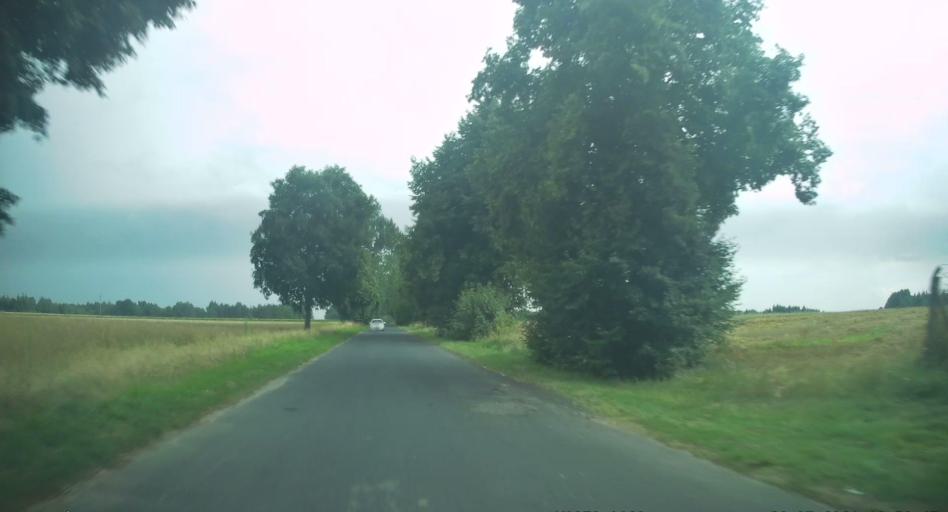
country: PL
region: Lodz Voivodeship
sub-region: Powiat rawski
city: Rawa Mazowiecka
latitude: 51.7649
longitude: 20.1846
